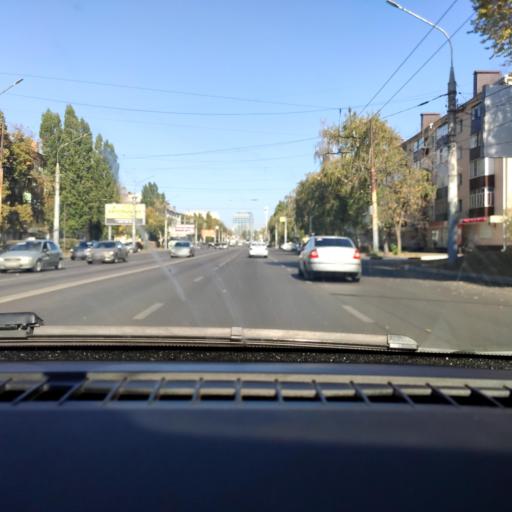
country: RU
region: Voronezj
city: Voronezh
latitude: 51.6656
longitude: 39.2492
